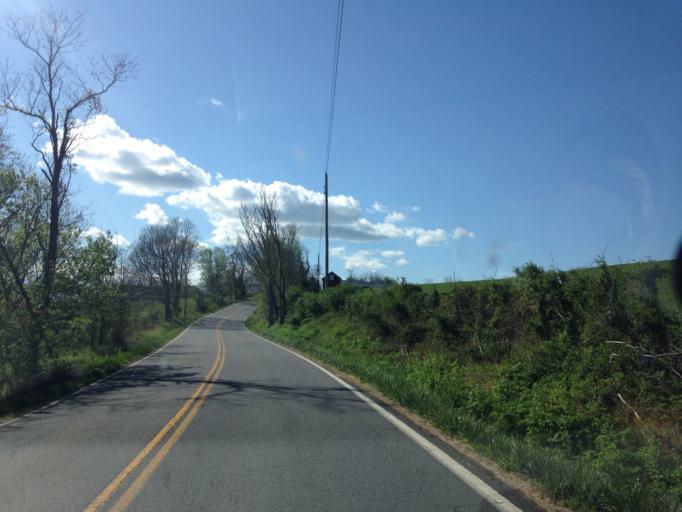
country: US
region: Maryland
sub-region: Frederick County
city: Point of Rocks
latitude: 39.2841
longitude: -77.5654
